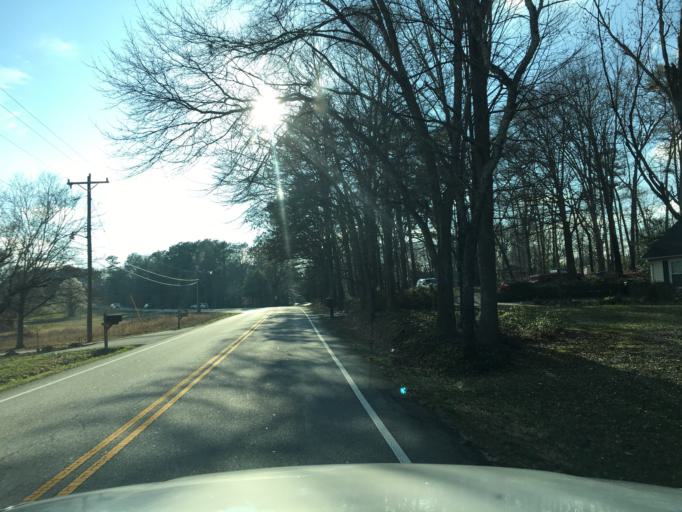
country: US
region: South Carolina
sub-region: Greenville County
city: Wade Hampton
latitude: 34.8743
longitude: -82.3076
